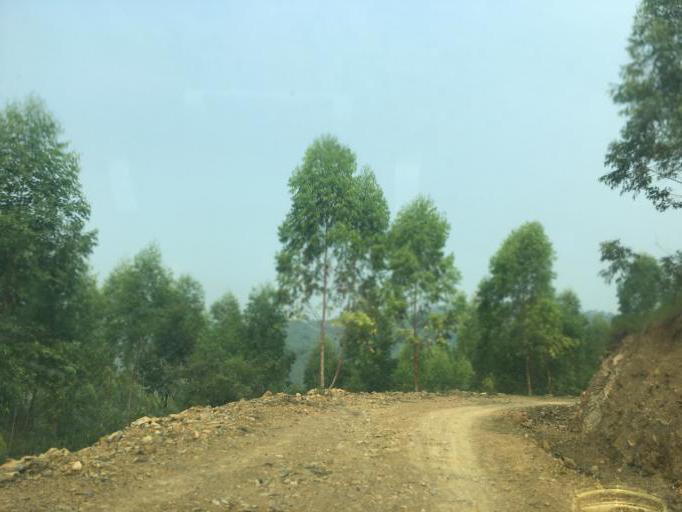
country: CN
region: Guizhou Sheng
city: Anshun
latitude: 25.4634
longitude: 105.9330
